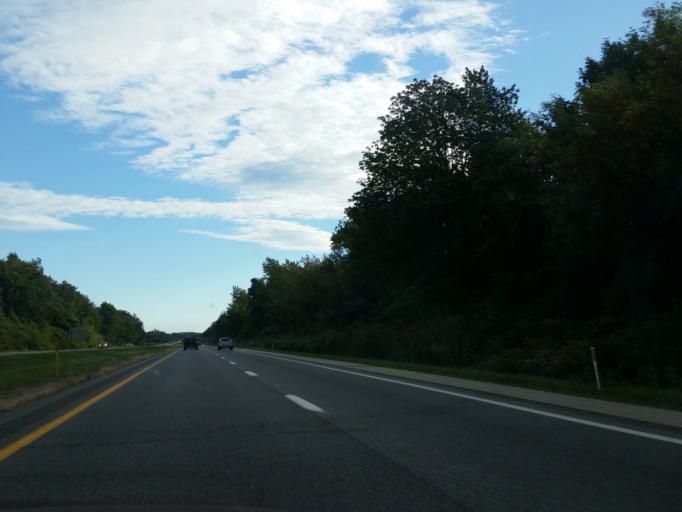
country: US
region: Pennsylvania
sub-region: Erie County
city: North East
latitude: 42.2098
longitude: -79.8034
